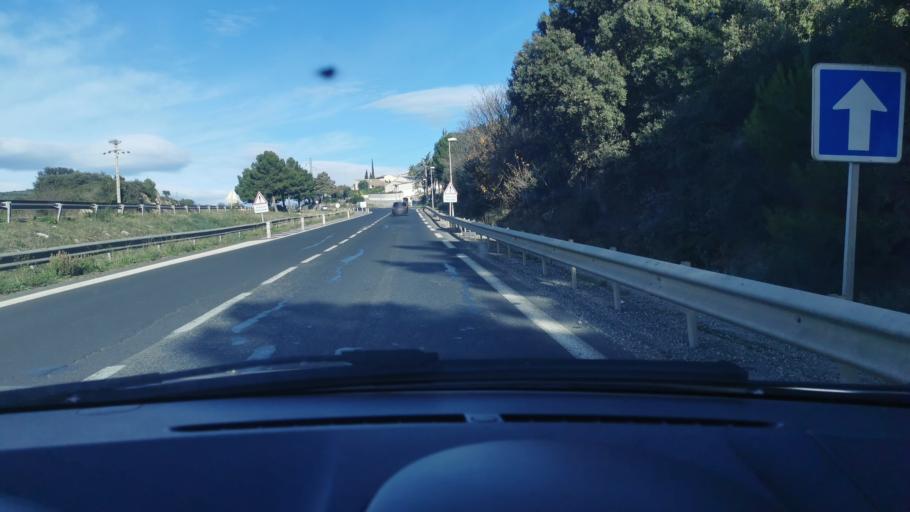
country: FR
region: Languedoc-Roussillon
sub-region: Departement de l'Herault
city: Mireval
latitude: 43.5165
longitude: 3.8076
